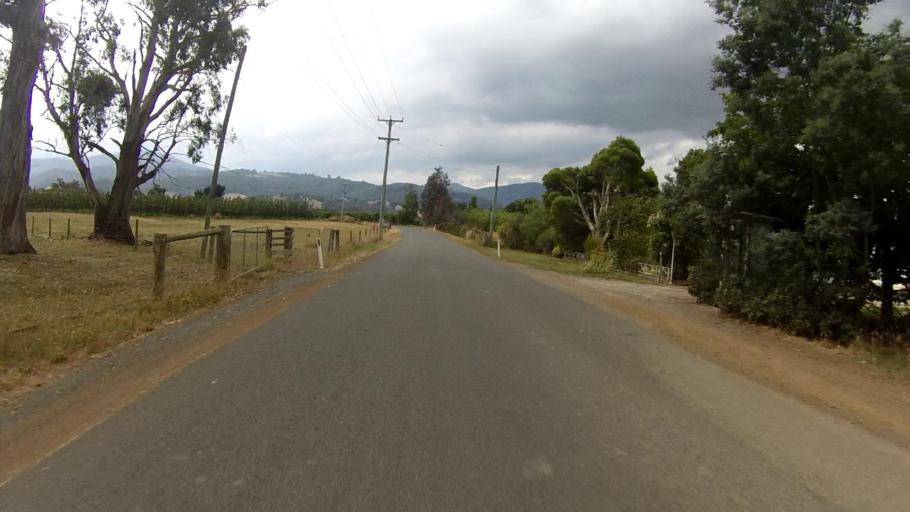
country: AU
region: Tasmania
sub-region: Huon Valley
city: Huonville
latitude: -42.9929
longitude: 147.0626
